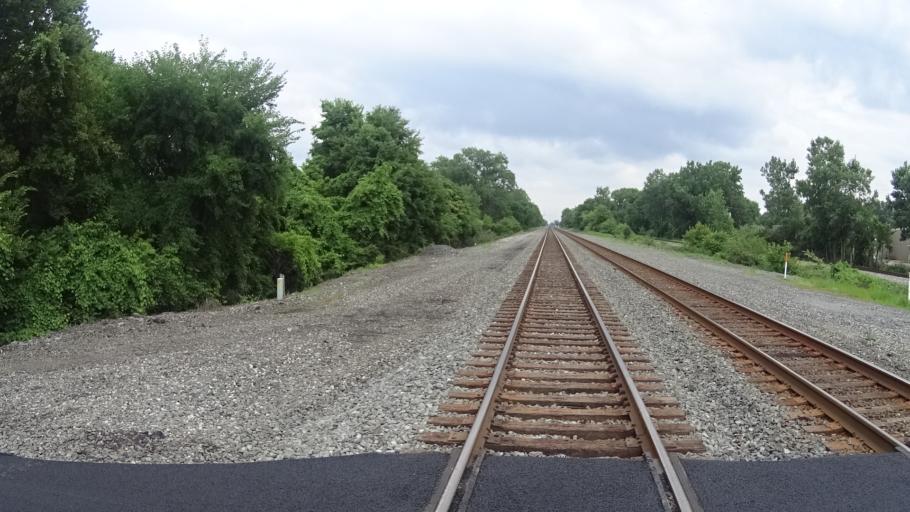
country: US
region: Ohio
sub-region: Erie County
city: Sandusky
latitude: 41.4423
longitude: -82.7376
